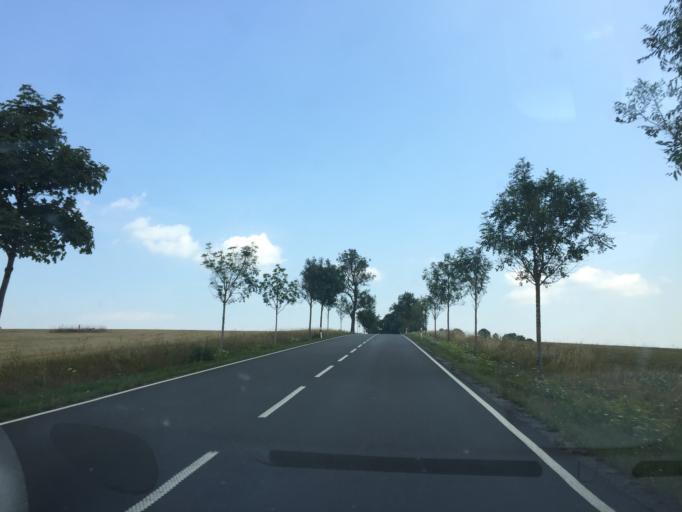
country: DE
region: Saxony-Anhalt
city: Elbingerode
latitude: 51.7507
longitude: 10.7749
